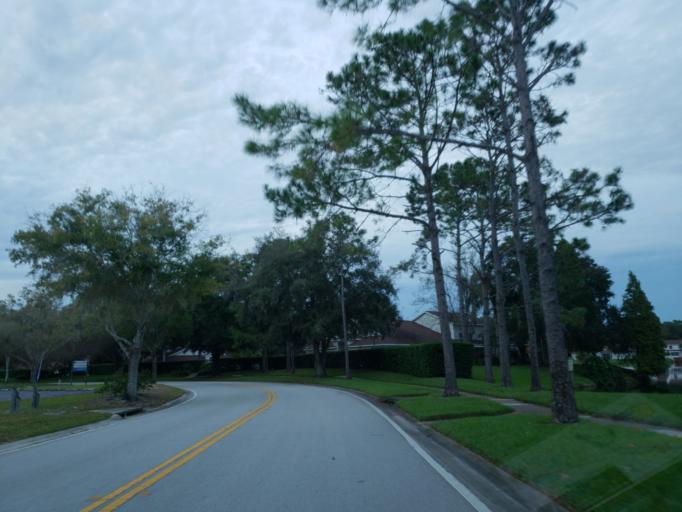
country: US
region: Florida
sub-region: Hillsborough County
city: Lutz
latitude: 28.1801
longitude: -82.4631
